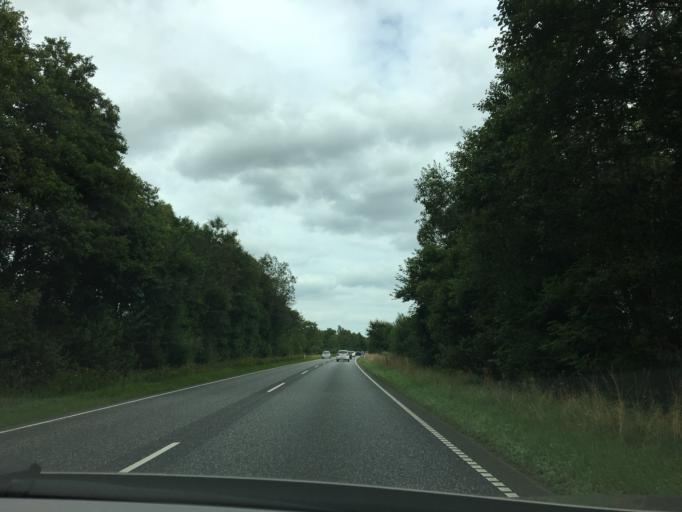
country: DK
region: South Denmark
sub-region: Vejle Kommune
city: Jelling
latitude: 55.7079
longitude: 9.4543
